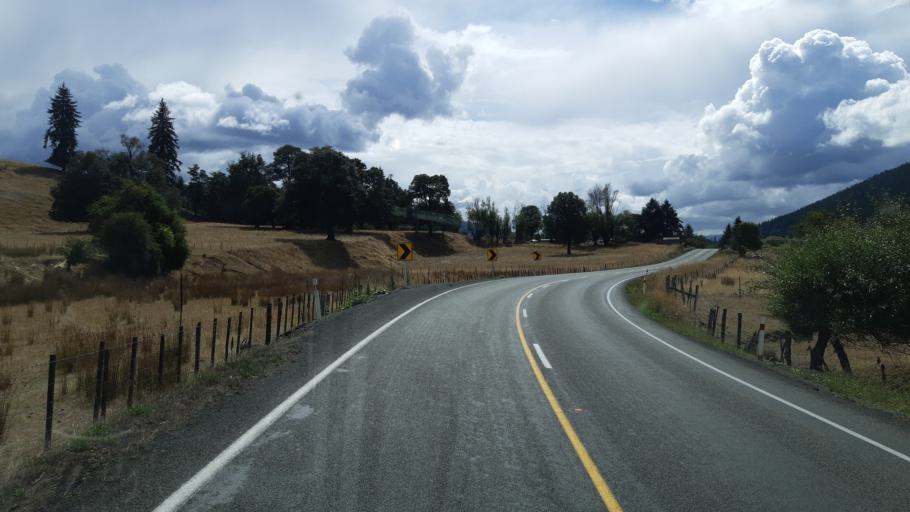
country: NZ
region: Tasman
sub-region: Tasman District
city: Wakefield
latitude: -41.4829
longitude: 172.7998
